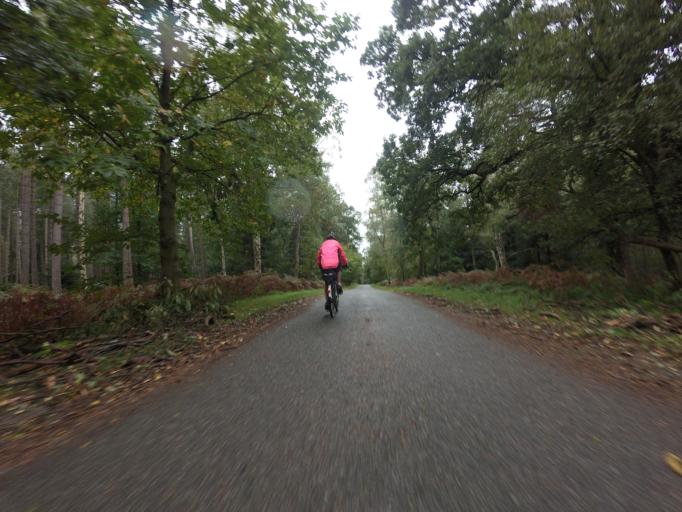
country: GB
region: England
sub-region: Norfolk
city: Dersingham
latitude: 52.8152
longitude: 0.4882
